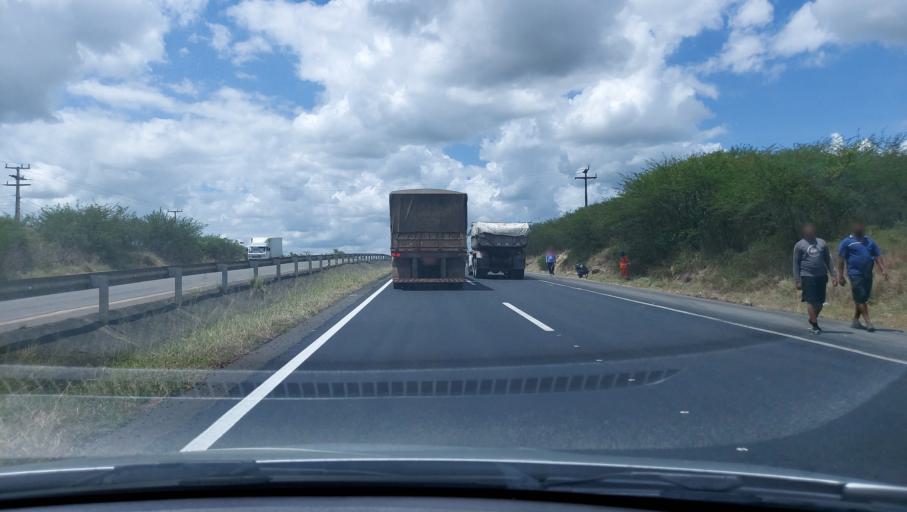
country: BR
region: Bahia
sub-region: Santo Estevao
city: Santo Estevao
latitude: -12.4255
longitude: -39.2058
